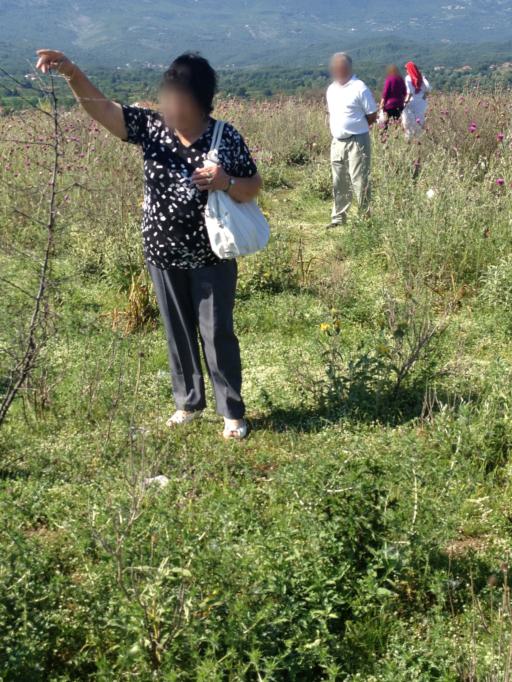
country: AL
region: Shkoder
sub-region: Rrethi i Shkodres
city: Dajc
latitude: 41.9868
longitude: 19.3177
